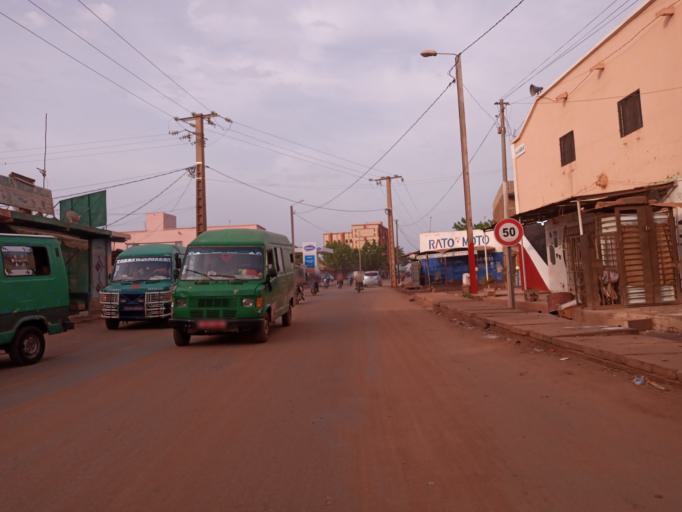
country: ML
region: Bamako
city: Bamako
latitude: 12.5821
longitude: -8.0237
